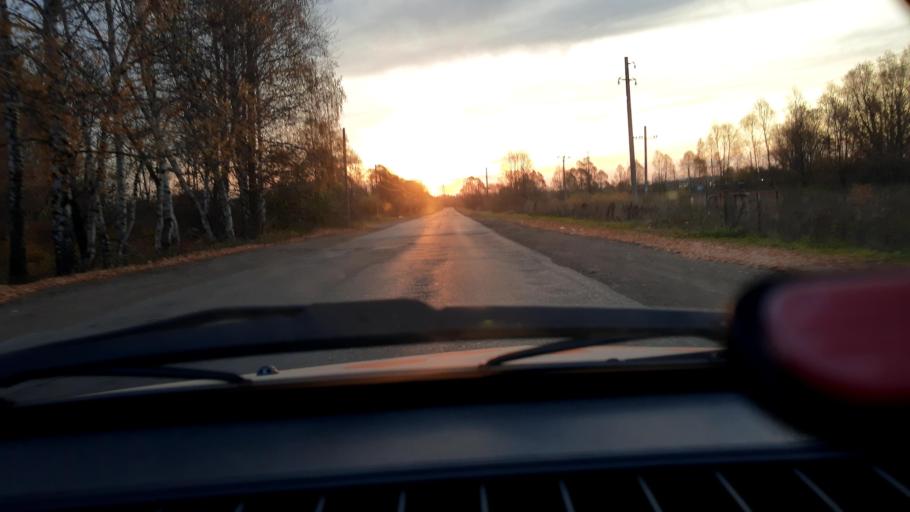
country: RU
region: Bashkortostan
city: Ufa
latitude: 54.8102
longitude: 56.1655
